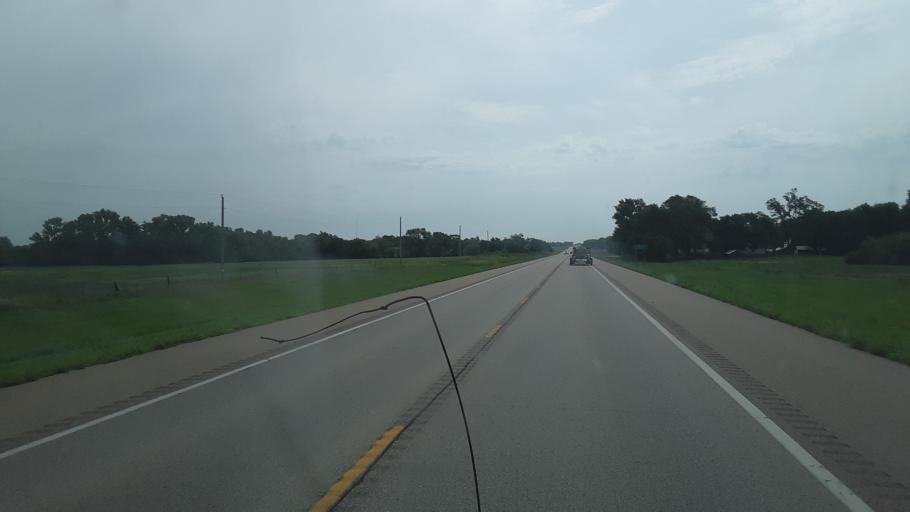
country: US
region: Kansas
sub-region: Stafford County
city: Stafford
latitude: 37.9843
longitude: -98.3420
